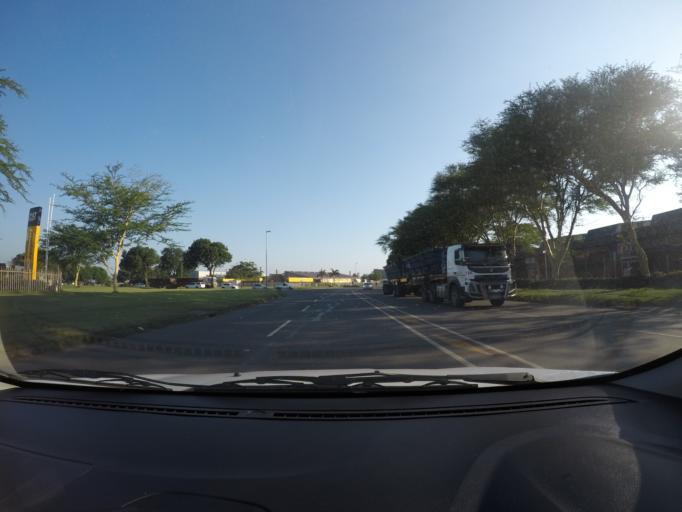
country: ZA
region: KwaZulu-Natal
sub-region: uThungulu District Municipality
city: Richards Bay
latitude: -28.7559
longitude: 32.0256
